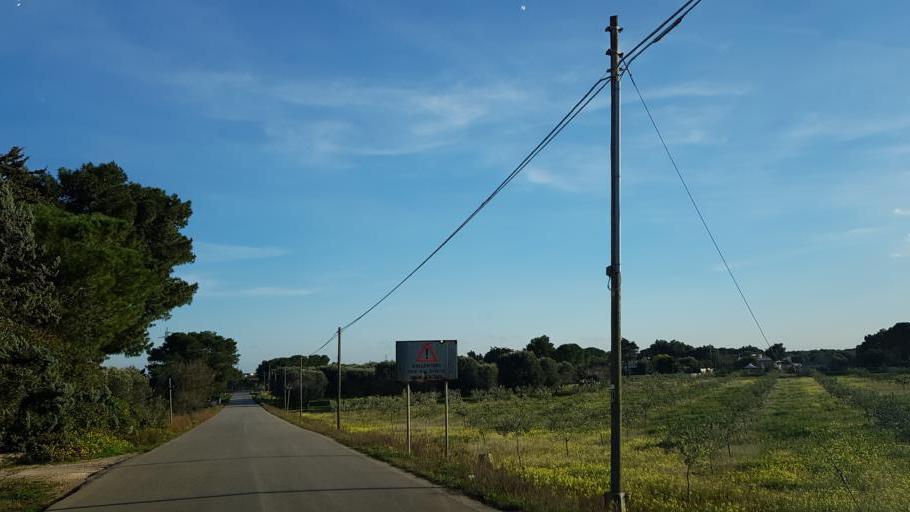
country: IT
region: Apulia
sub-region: Provincia di Brindisi
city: San Vito dei Normanni
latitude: 40.6795
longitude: 17.7730
